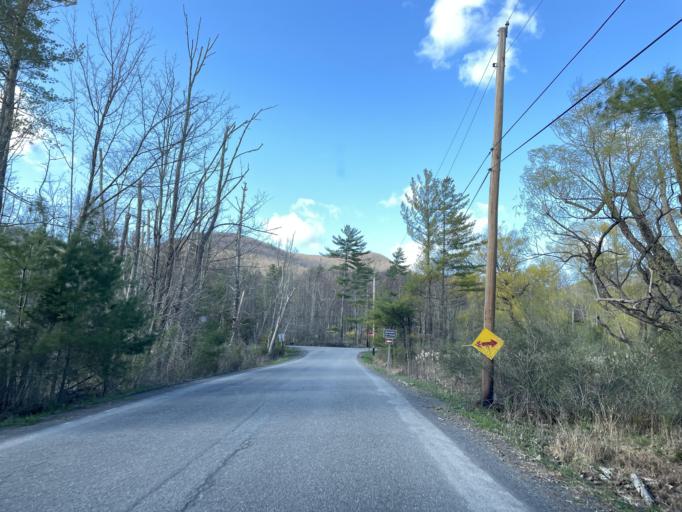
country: US
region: New York
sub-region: Ulster County
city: Woodstock
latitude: 42.0500
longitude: -74.1383
